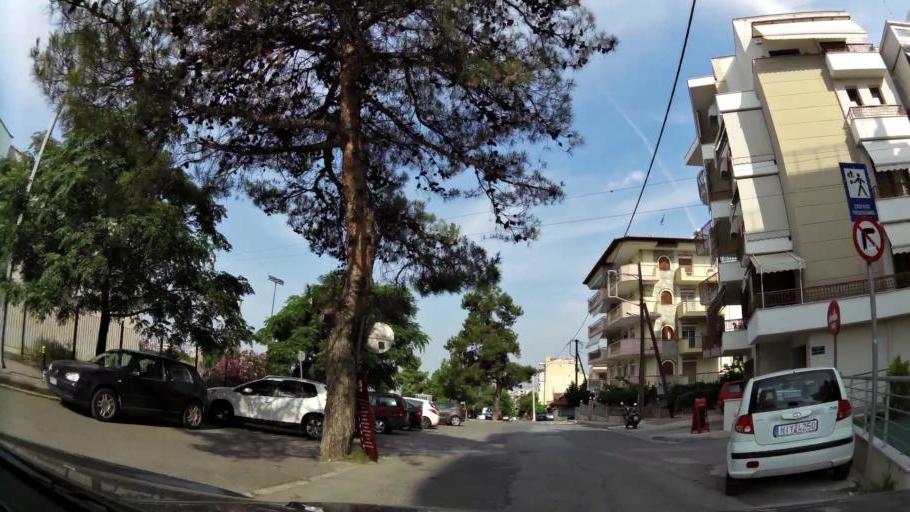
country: GR
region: Central Macedonia
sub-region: Nomos Thessalonikis
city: Sykies
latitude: 40.6574
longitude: 22.9470
